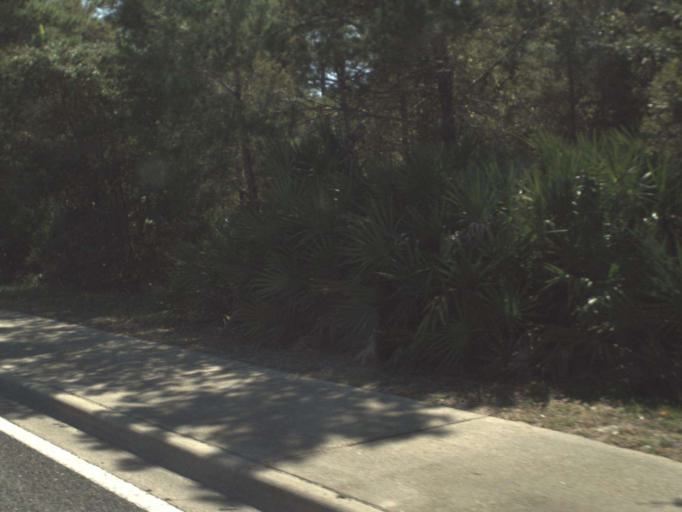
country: US
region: Florida
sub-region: Walton County
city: Miramar Beach
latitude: 30.3785
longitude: -86.3164
